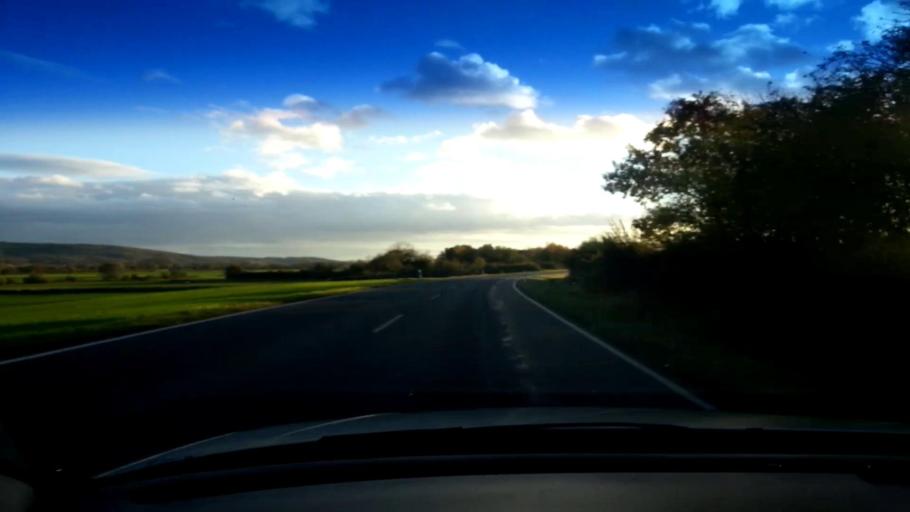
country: DE
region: Bavaria
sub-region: Upper Franconia
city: Zapfendorf
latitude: 50.0383
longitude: 10.9173
